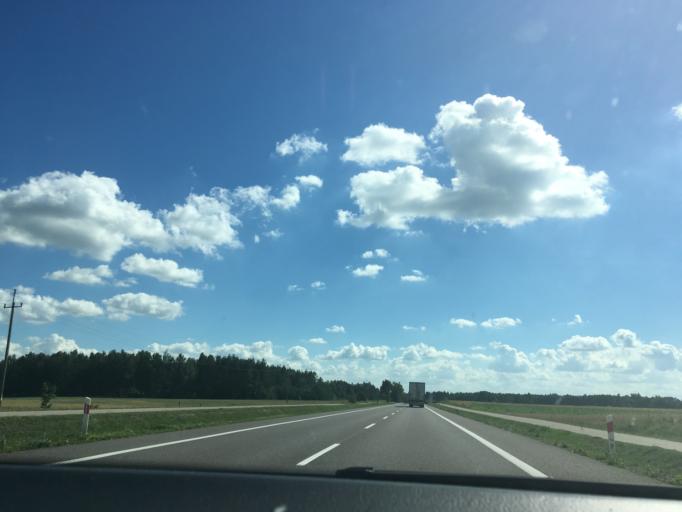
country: PL
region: Podlasie
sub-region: Powiat sokolski
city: Suchowola
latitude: 53.7040
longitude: 23.0959
